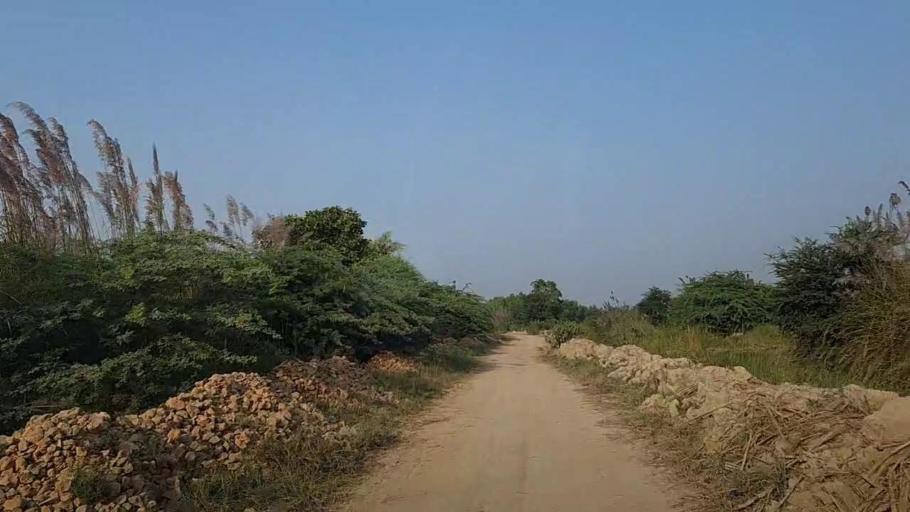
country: PK
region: Sindh
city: Thatta
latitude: 24.6591
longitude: 67.7712
